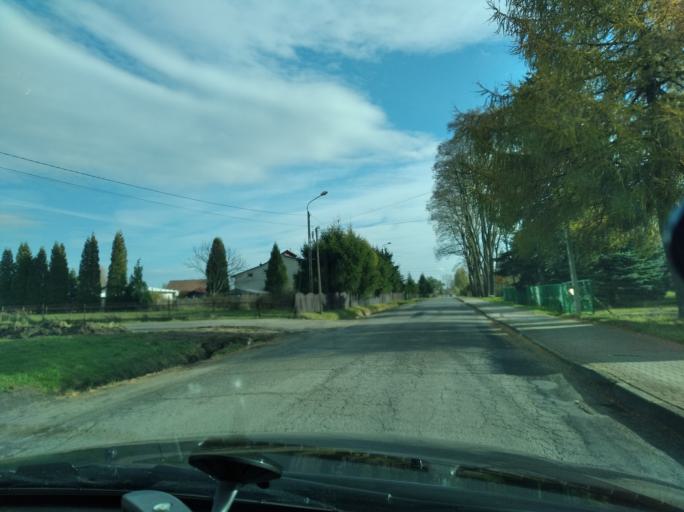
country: PL
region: Subcarpathian Voivodeship
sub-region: Powiat ropczycko-sedziszowski
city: Ostrow
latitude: 50.0994
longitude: 21.6161
